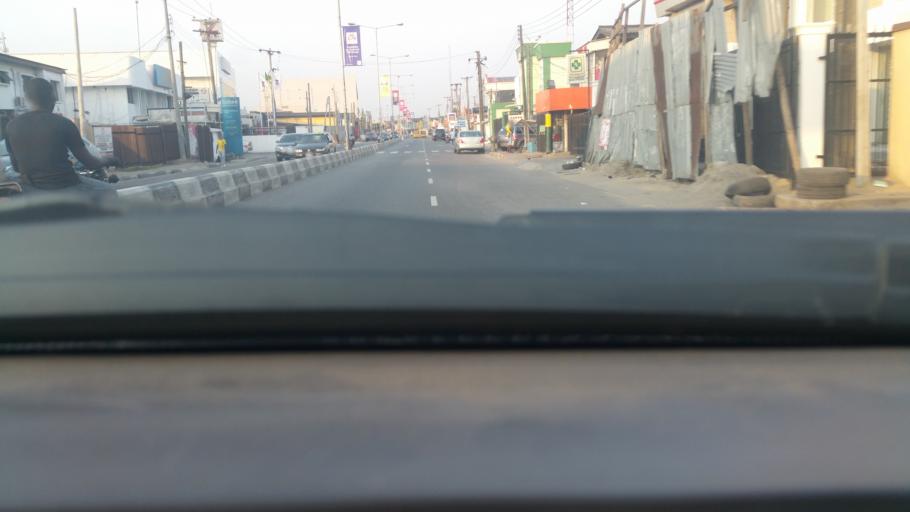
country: NG
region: Lagos
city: Surulere
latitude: 6.4938
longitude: 3.3572
